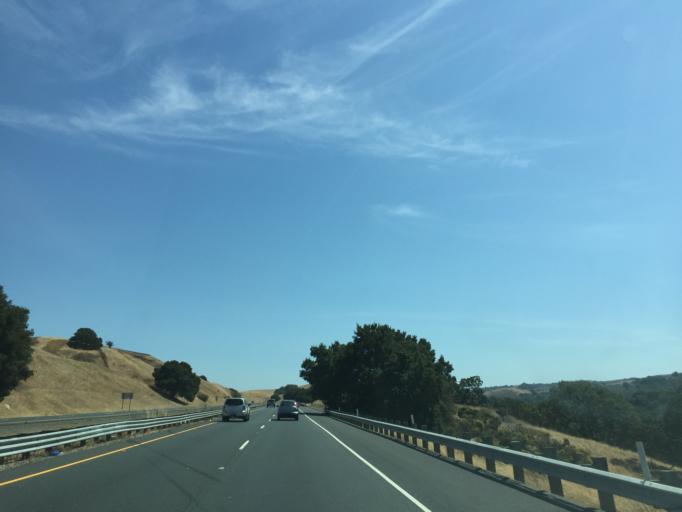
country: US
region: California
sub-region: Contra Costa County
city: Martinez
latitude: 38.0109
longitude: -122.1720
